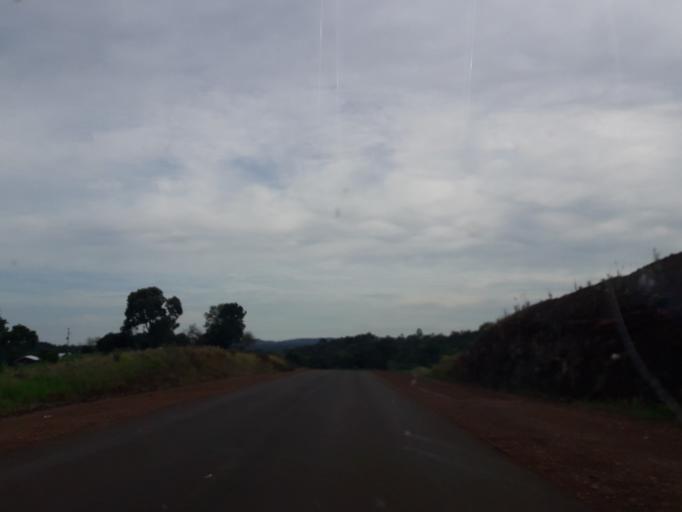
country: AR
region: Misiones
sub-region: Departamento de San Pedro
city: San Pedro
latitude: -26.5211
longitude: -53.9392
